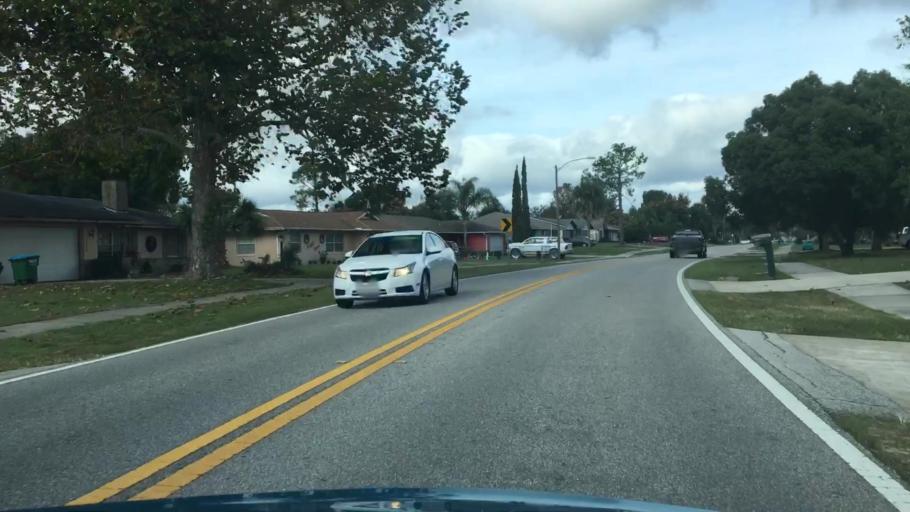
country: US
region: Florida
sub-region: Volusia County
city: Deltona
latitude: 28.8863
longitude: -81.2433
